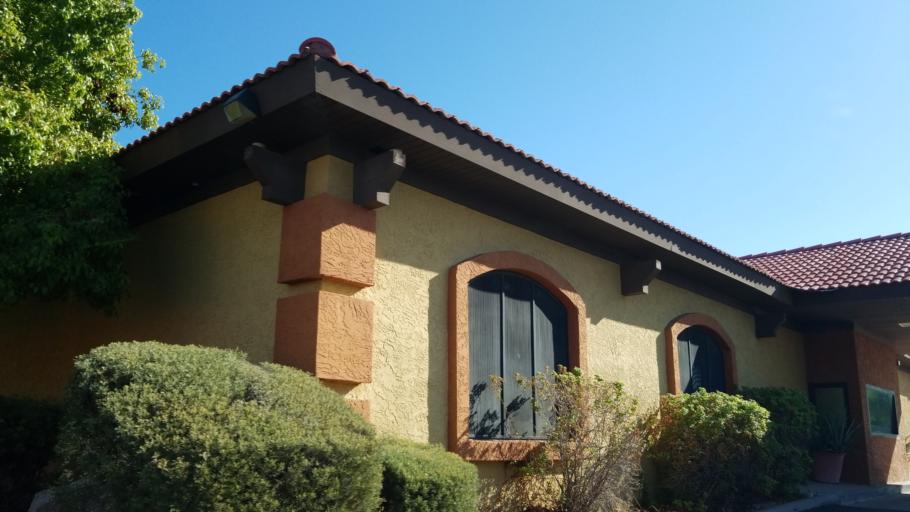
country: US
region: Arizona
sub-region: Maricopa County
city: Avondale
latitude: 33.4494
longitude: -112.3503
